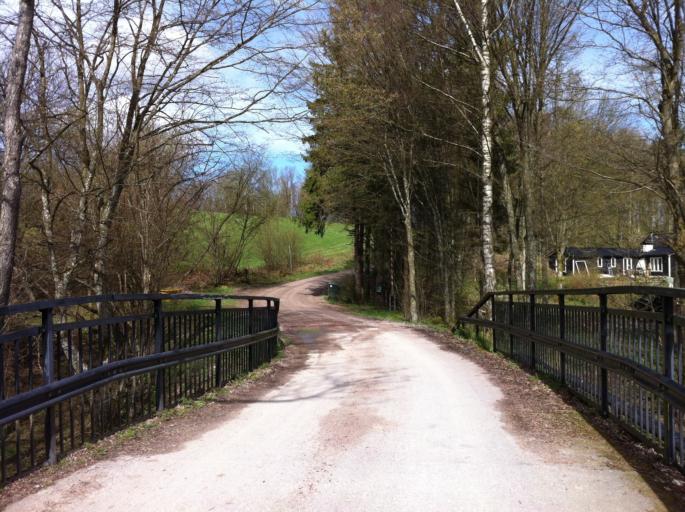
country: SE
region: Skane
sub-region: Perstorps Kommun
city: Perstorp
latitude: 56.0210
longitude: 13.3876
